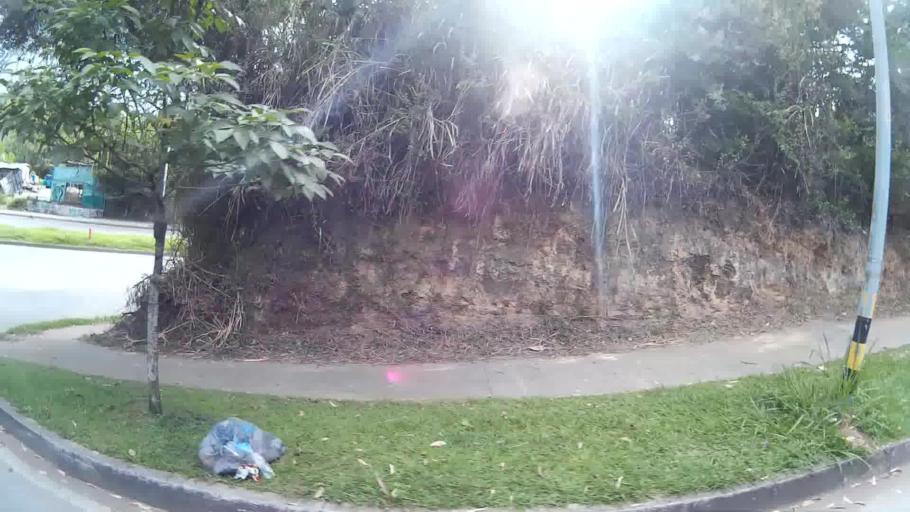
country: CO
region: Risaralda
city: Pereira
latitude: 4.8029
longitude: -75.7594
